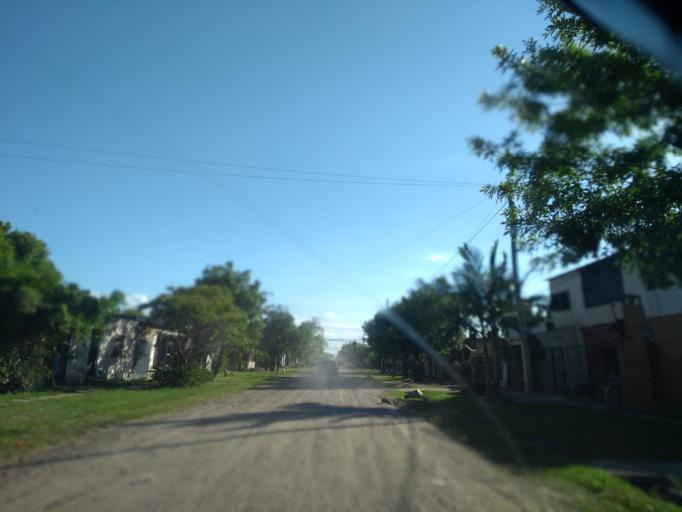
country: AR
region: Chaco
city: Resistencia
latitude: -27.4762
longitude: -58.9699
